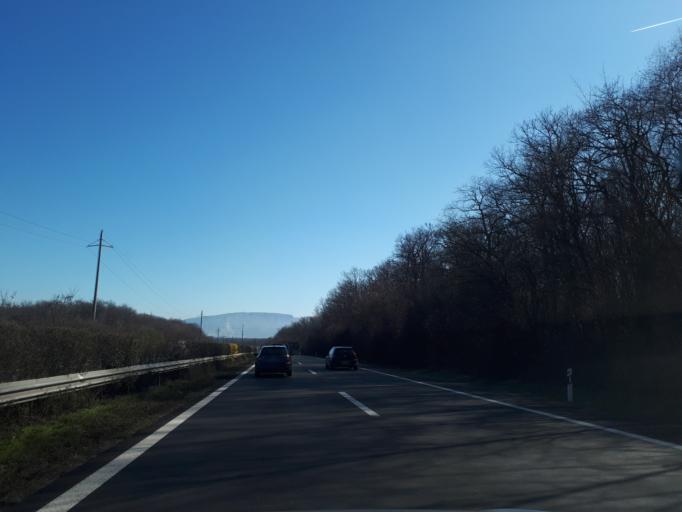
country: CH
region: Geneva
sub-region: Geneva
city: Versoix
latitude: 46.3049
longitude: 6.1438
